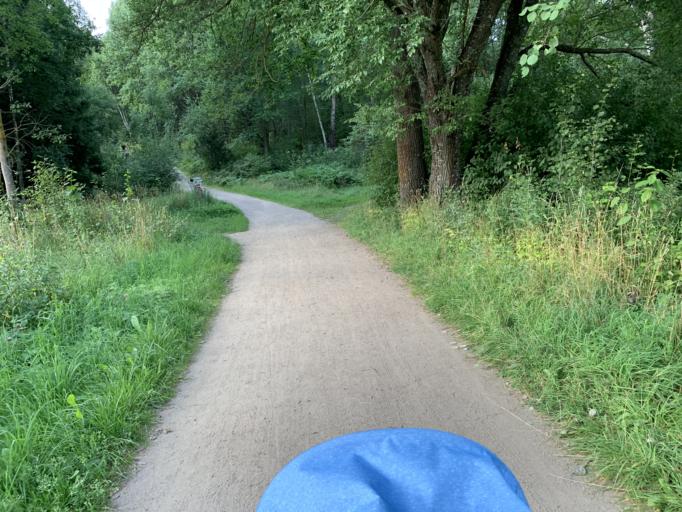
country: SE
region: Stockholm
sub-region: Solna Kommun
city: Rasunda
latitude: 59.3914
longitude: 17.9866
